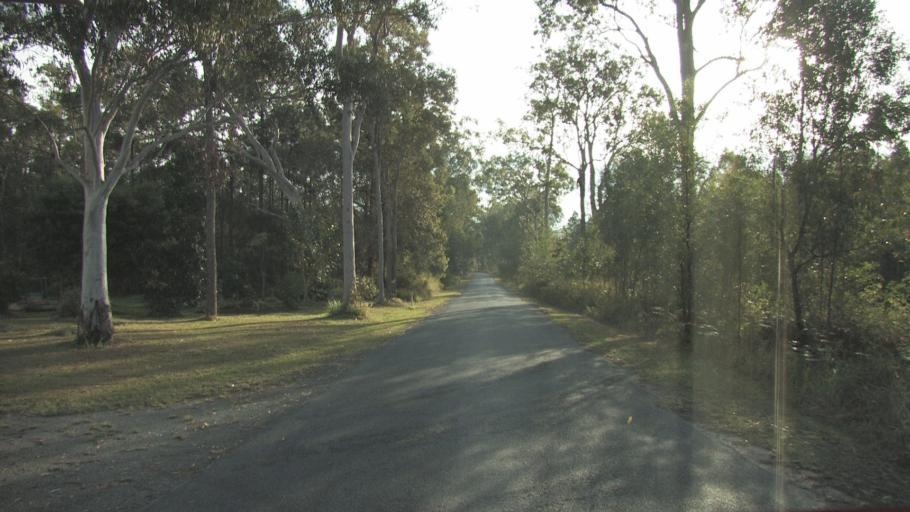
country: AU
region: Queensland
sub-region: Logan
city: Chambers Flat
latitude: -27.8384
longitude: 153.1157
